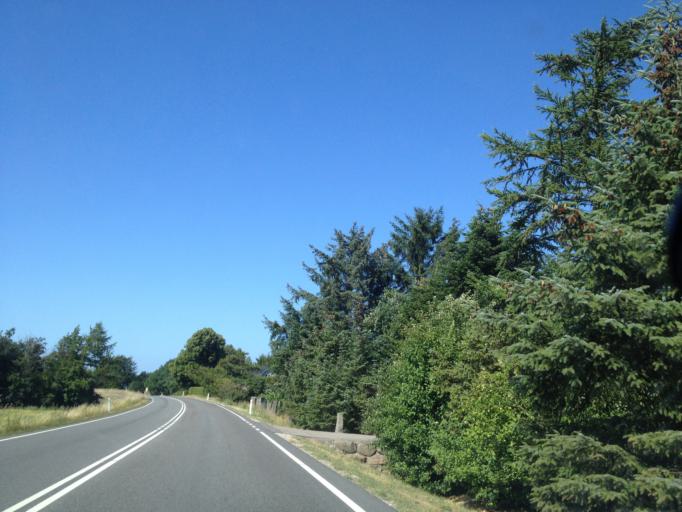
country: DK
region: Capital Region
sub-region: Gribskov Kommune
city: Graested
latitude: 56.0583
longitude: 12.3416
